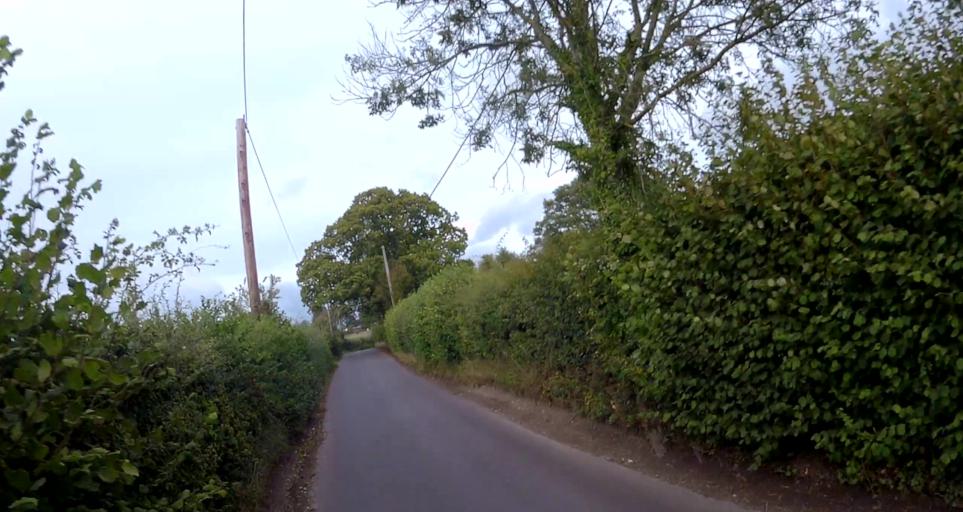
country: GB
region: England
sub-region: Hampshire
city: Four Marks
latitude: 51.1274
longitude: -1.0751
